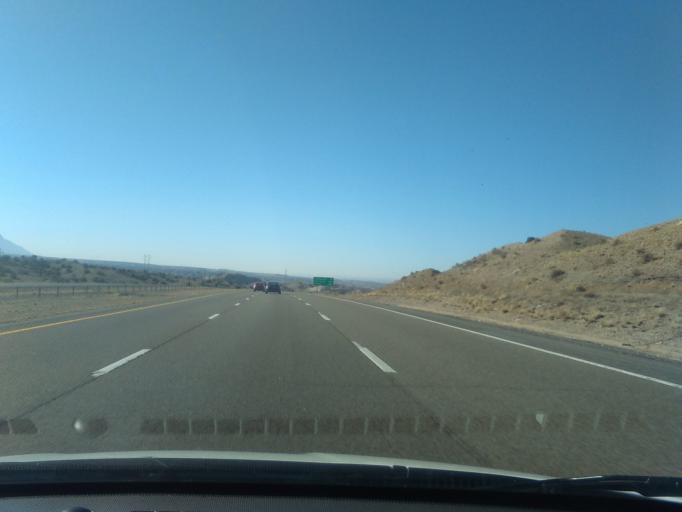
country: US
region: New Mexico
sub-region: Sandoval County
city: San Felipe Pueblo
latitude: 35.4111
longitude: -106.4170
